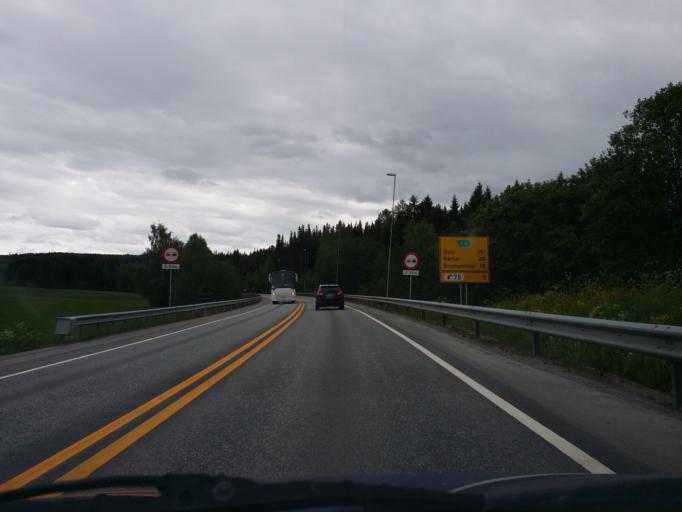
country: NO
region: Hedmark
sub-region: Ringsaker
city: Moelv
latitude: 60.9106
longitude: 10.7226
